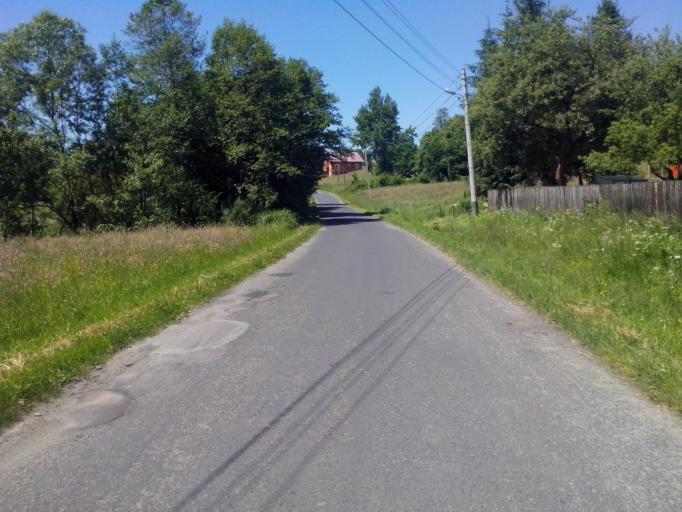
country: PL
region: Subcarpathian Voivodeship
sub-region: Powiat krosnienski
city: Leki
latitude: 49.8051
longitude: 21.6932
